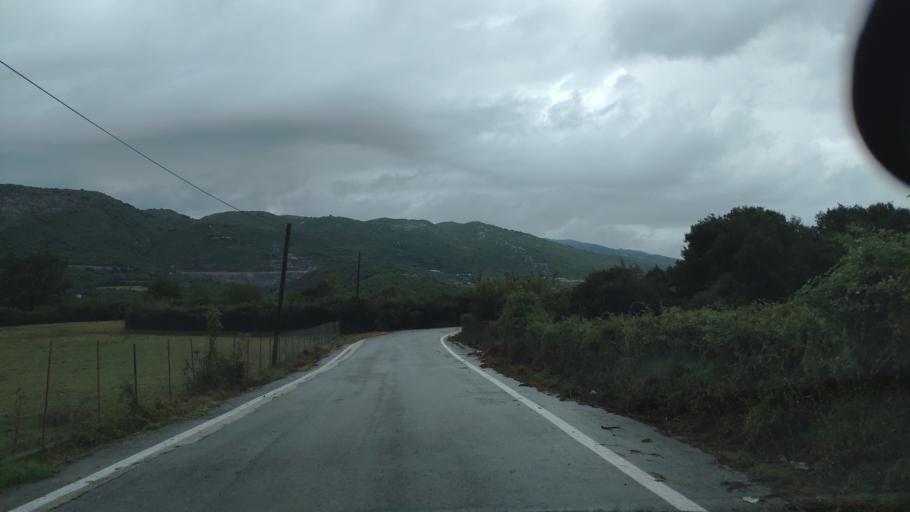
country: GR
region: Central Greece
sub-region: Nomos Evrytanias
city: Kerasochori
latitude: 39.1028
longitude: 21.4284
